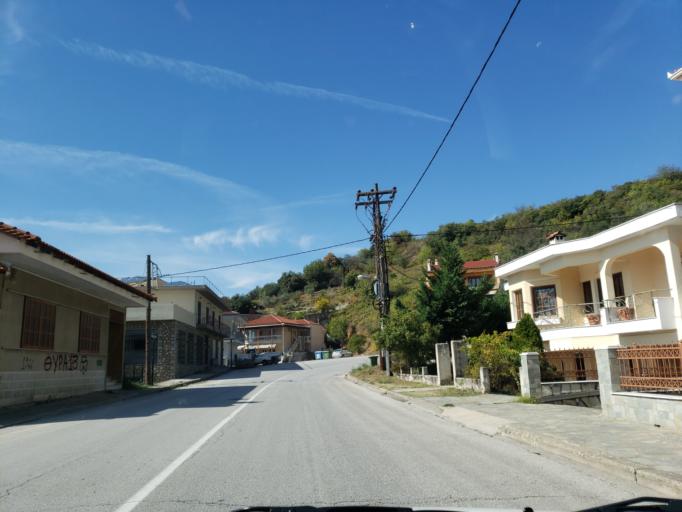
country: GR
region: Thessaly
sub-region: Trikala
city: Kastraki
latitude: 39.7080
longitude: 21.6185
